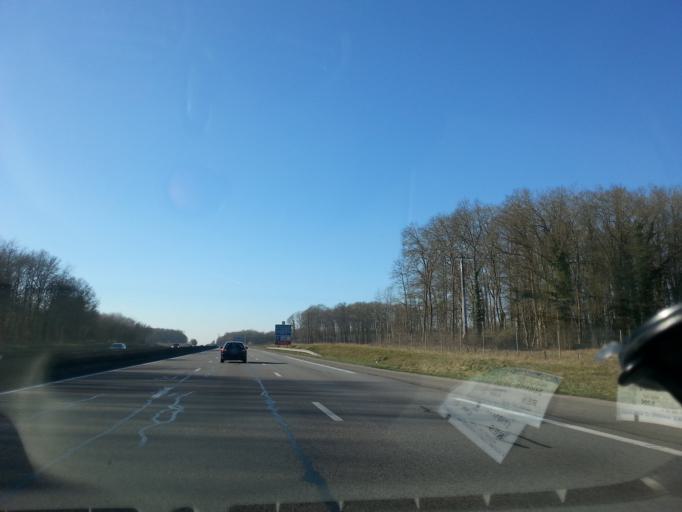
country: FR
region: Ile-de-France
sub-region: Departement des Yvelines
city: Bennecourt
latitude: 49.0212
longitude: 1.5567
